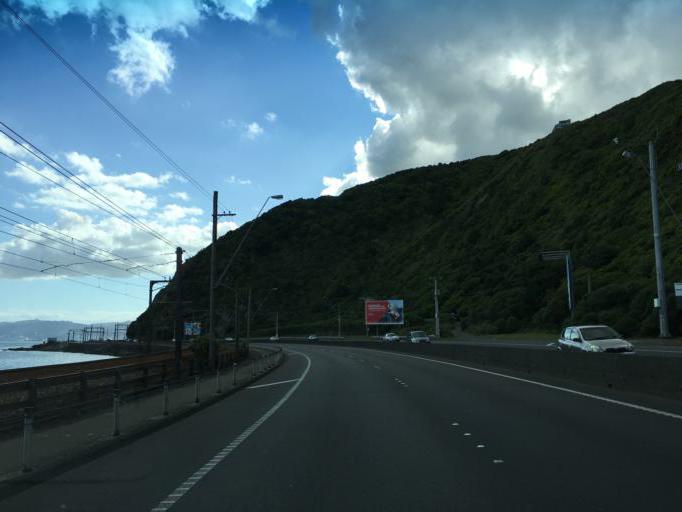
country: NZ
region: Wellington
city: Petone
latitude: -41.2284
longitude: 174.8448
